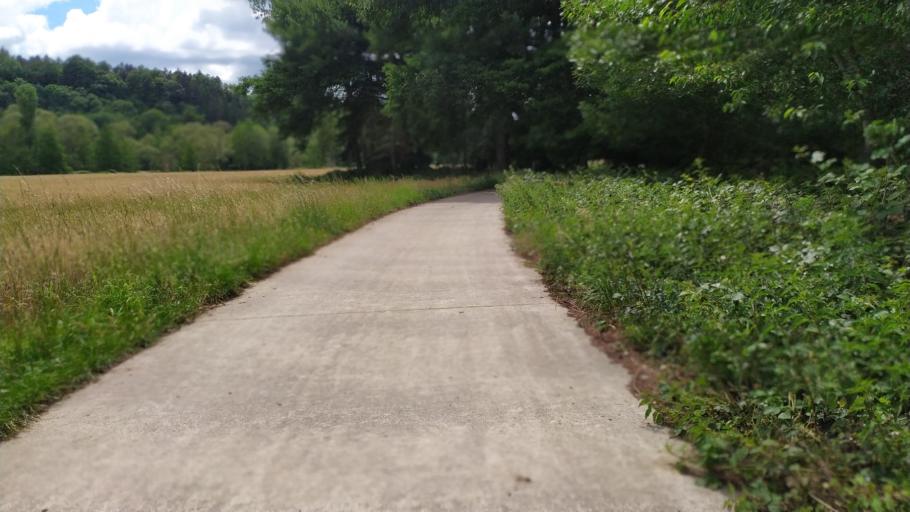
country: BE
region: Wallonia
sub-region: Province du Luxembourg
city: Wellin
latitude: 50.1645
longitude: 5.0947
